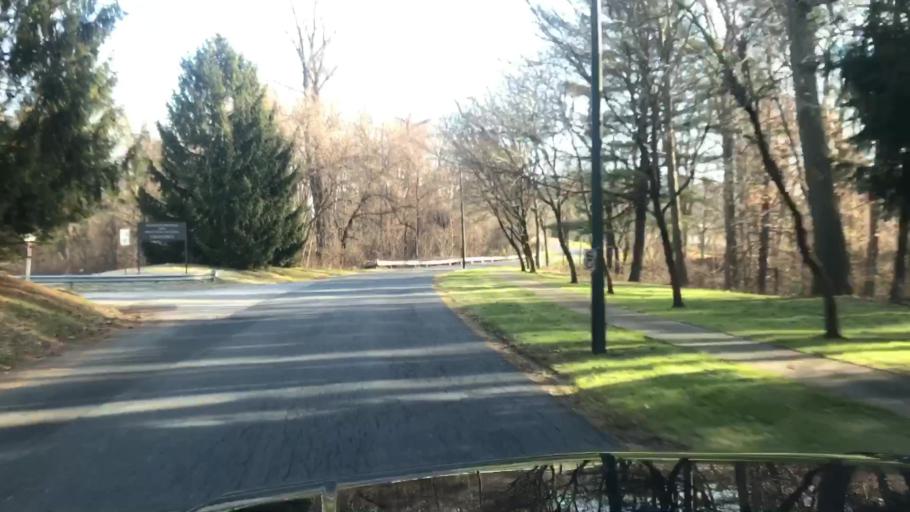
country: US
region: Pennsylvania
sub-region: Dauphin County
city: Harrisburg
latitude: 40.2868
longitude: -76.8764
